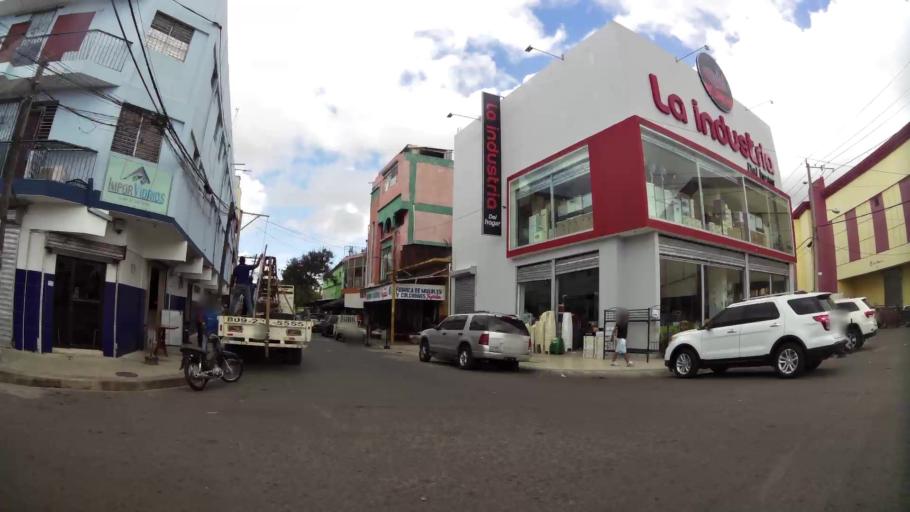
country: DO
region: Nacional
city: San Carlos
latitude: 18.4877
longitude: -69.8971
